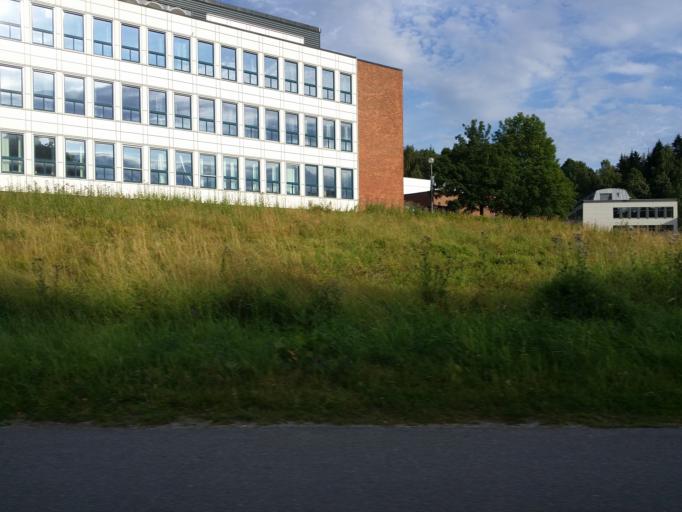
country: NO
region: Akershus
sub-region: Oppegard
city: Kolbotn
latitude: 59.8853
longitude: 10.8492
